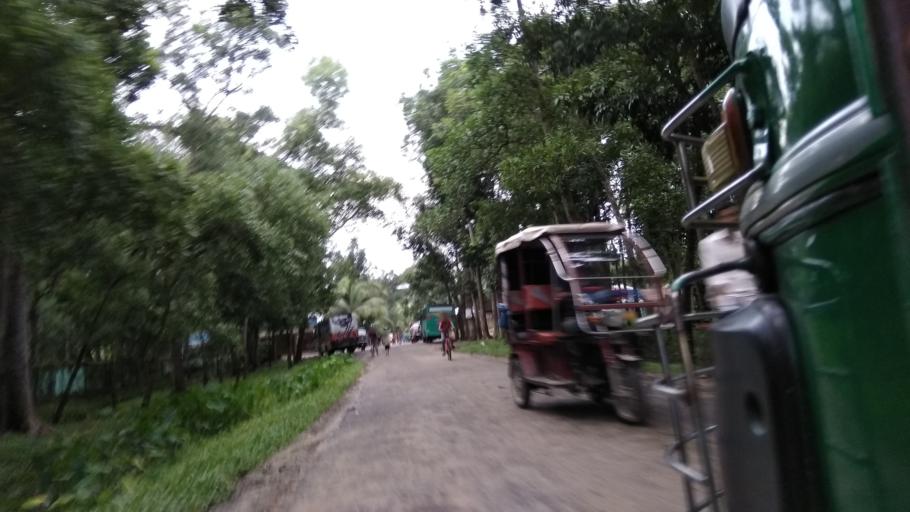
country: IN
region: Tripura
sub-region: Dhalai
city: Kamalpur
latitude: 24.2070
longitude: 91.8649
